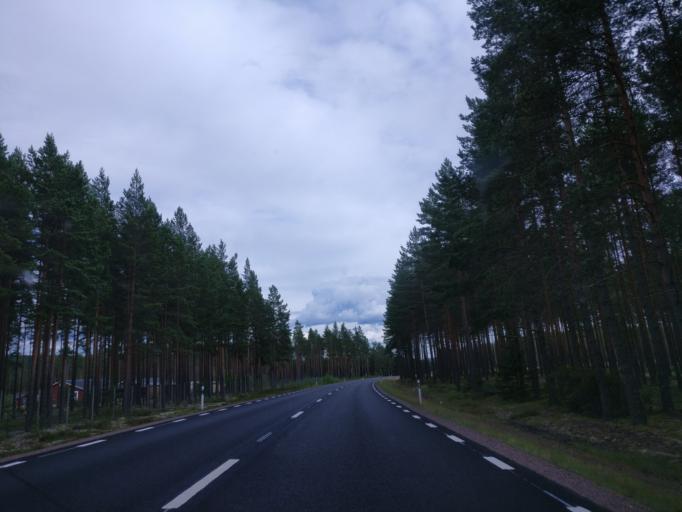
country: SE
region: Vaermland
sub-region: Hagfors Kommun
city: Hagfors
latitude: 60.0468
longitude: 13.5757
